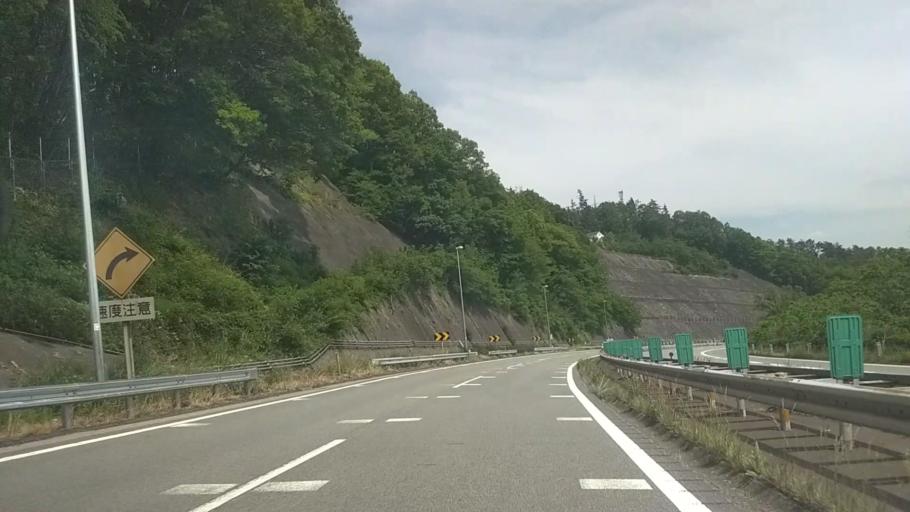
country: JP
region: Yamanashi
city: Nirasaki
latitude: 35.7921
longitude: 138.4058
